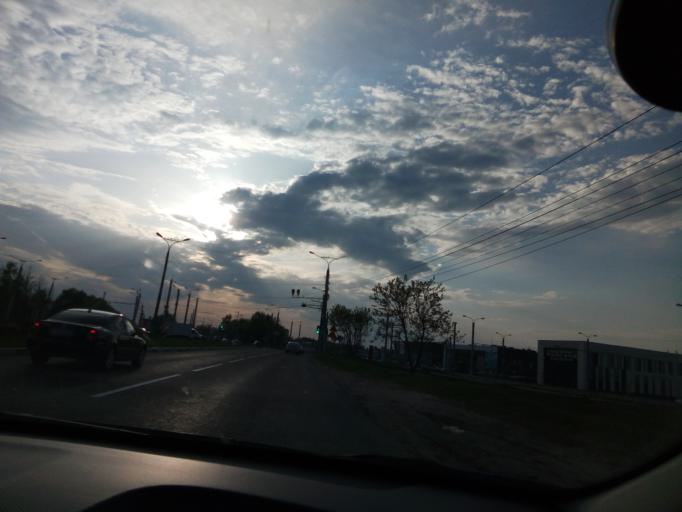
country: RU
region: Chuvashia
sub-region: Cheboksarskiy Rayon
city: Cheboksary
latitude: 56.1257
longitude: 47.3650
